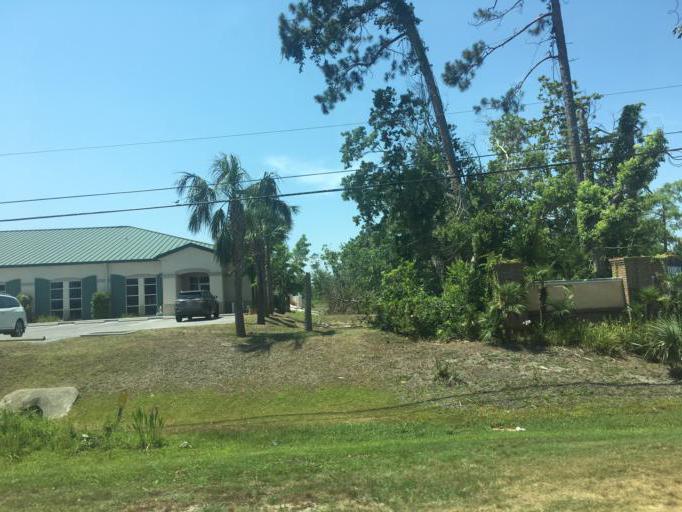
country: US
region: Florida
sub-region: Bay County
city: Lynn Haven
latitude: 30.2187
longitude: -85.6513
